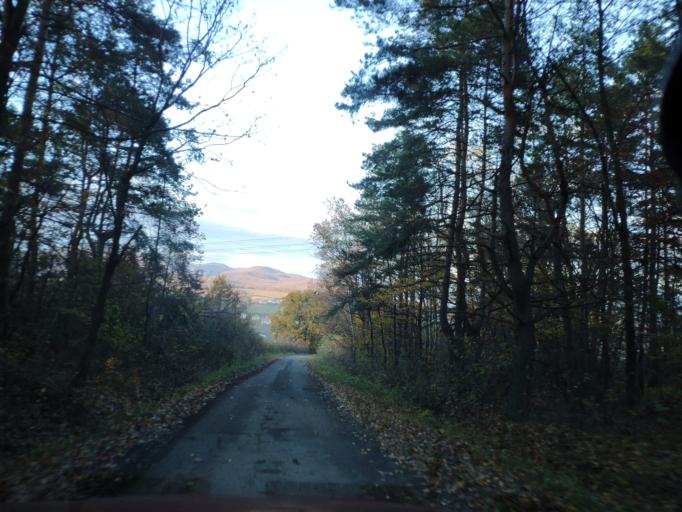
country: SK
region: Kosicky
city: Secovce
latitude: 48.6083
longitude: 21.5198
